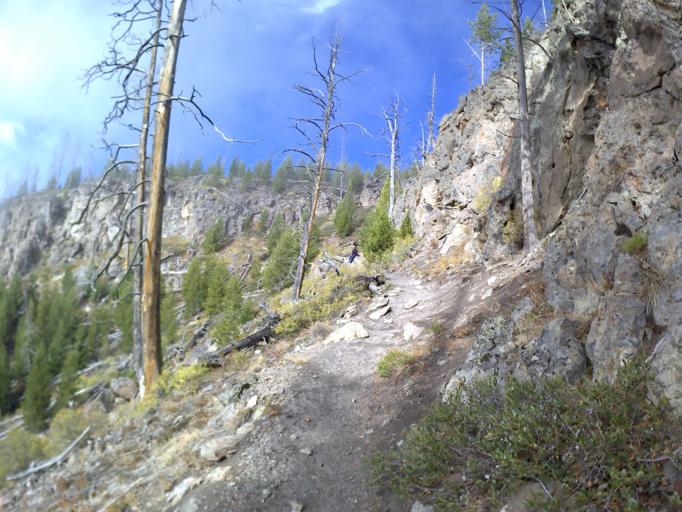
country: US
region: Montana
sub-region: Gallatin County
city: West Yellowstone
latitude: 44.4866
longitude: -110.8678
